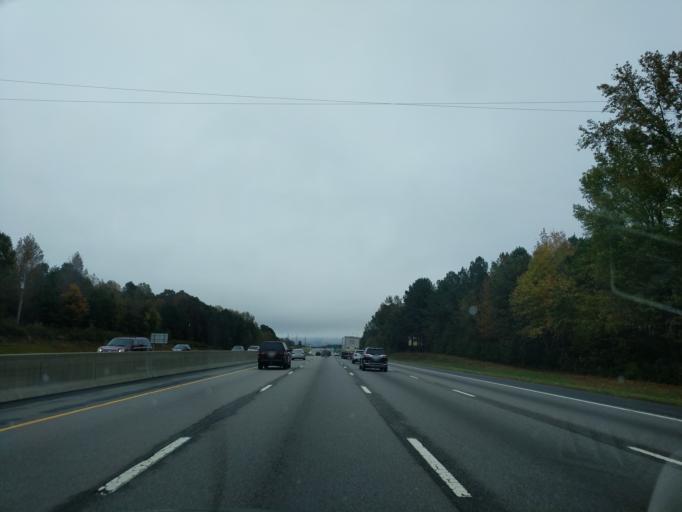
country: US
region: North Carolina
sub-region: Orange County
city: Hillsborough
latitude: 36.0739
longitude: -79.1811
